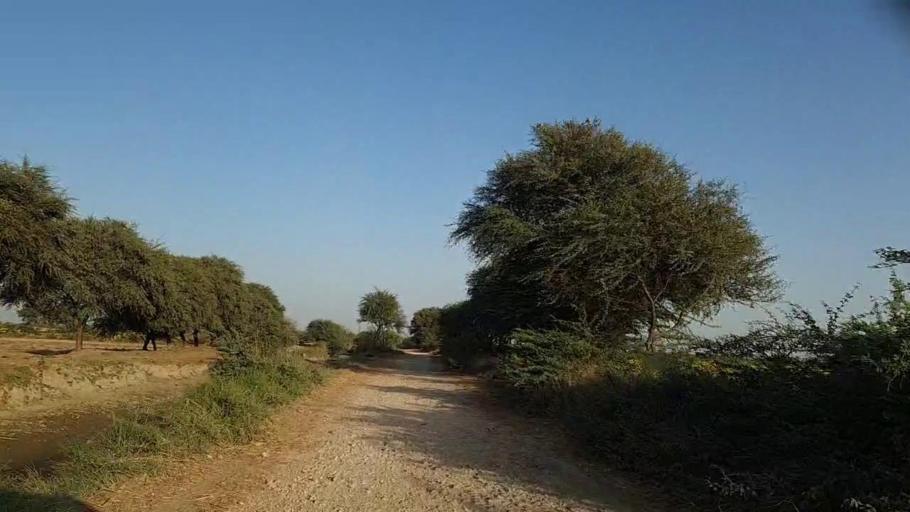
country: PK
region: Sindh
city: Jati
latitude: 24.4140
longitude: 68.3249
